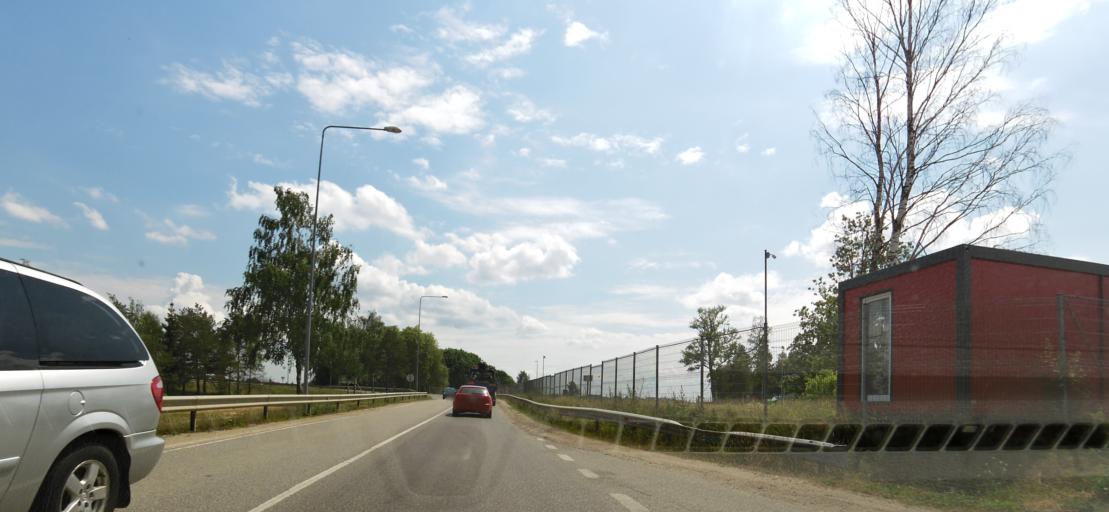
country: LT
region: Vilnius County
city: Pasilaiciai
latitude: 54.7630
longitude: 25.1986
